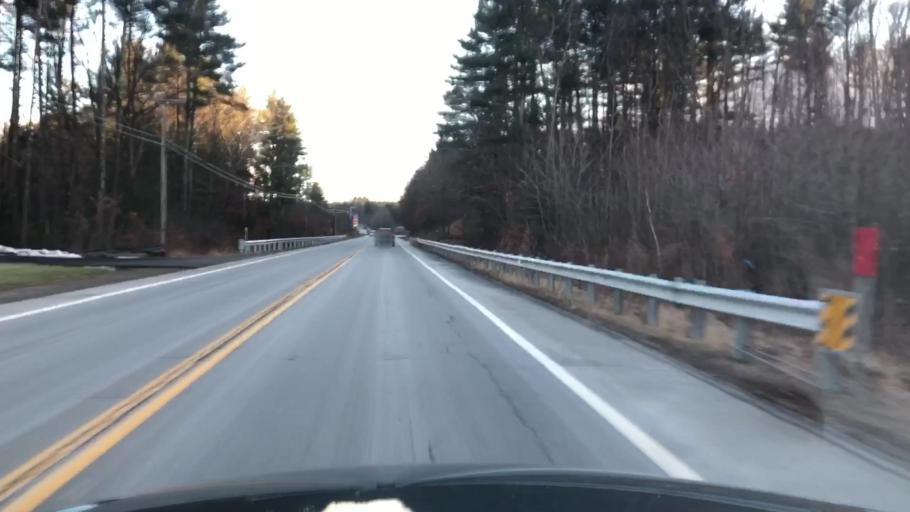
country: US
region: New Hampshire
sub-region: Hillsborough County
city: Brookline
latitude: 42.7262
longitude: -71.6632
